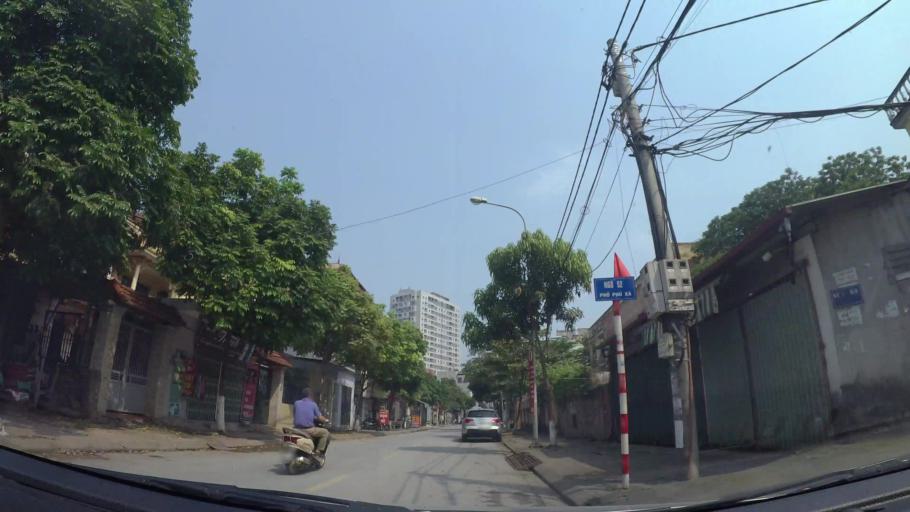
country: VN
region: Ha Noi
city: Tay Ho
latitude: 21.0879
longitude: 105.8121
